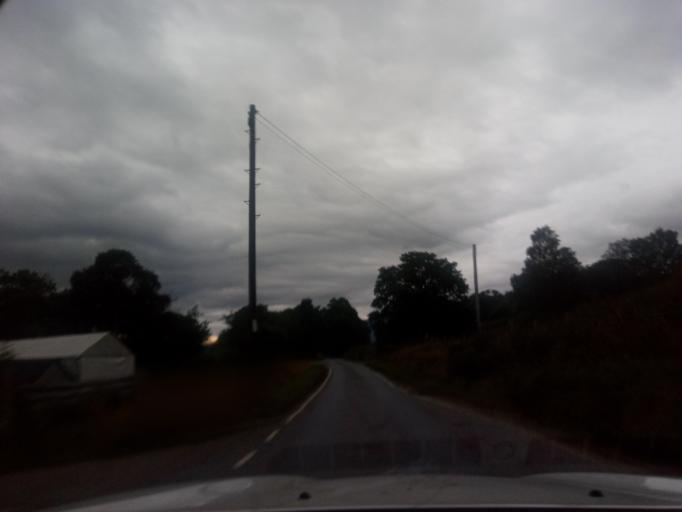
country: GB
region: Scotland
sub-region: Highland
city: Fort William
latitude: 56.8470
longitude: -5.2982
